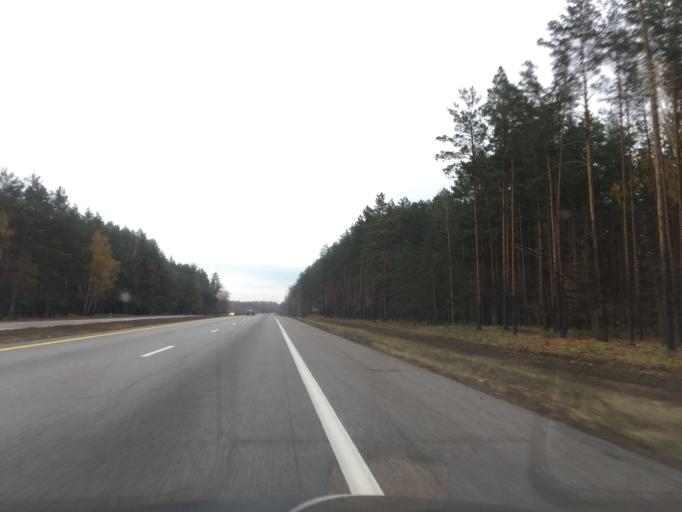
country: BY
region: Gomel
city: Gomel
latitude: 52.3651
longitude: 30.7402
